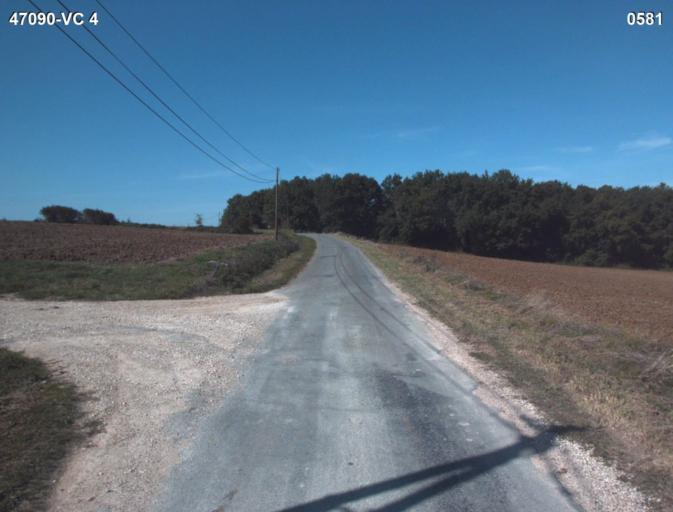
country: FR
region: Aquitaine
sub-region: Departement du Lot-et-Garonne
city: Vianne
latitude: 44.1769
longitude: 0.3498
